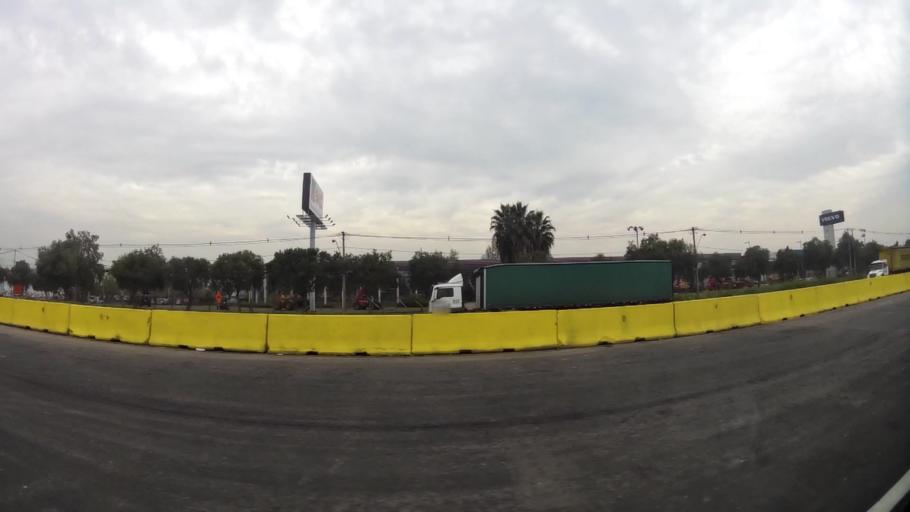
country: CL
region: Santiago Metropolitan
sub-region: Provincia de Chacabuco
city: Chicureo Abajo
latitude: -33.3219
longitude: -70.7200
